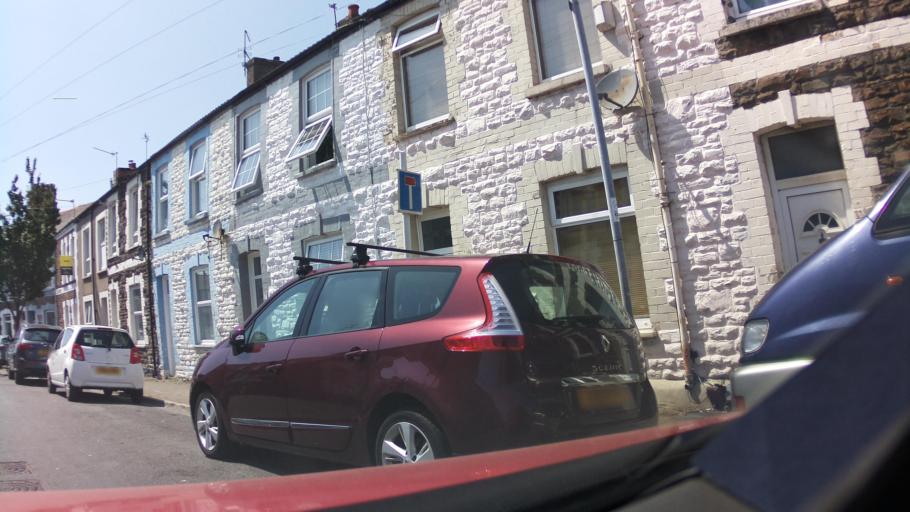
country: GB
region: Wales
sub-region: Cardiff
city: Cardiff
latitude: 51.4821
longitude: -3.1560
